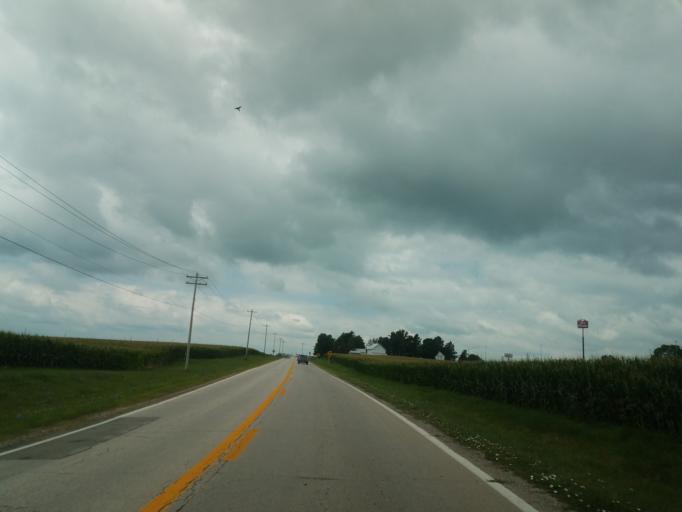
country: US
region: Illinois
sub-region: McLean County
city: Bloomington
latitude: 40.4844
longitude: -89.0329
